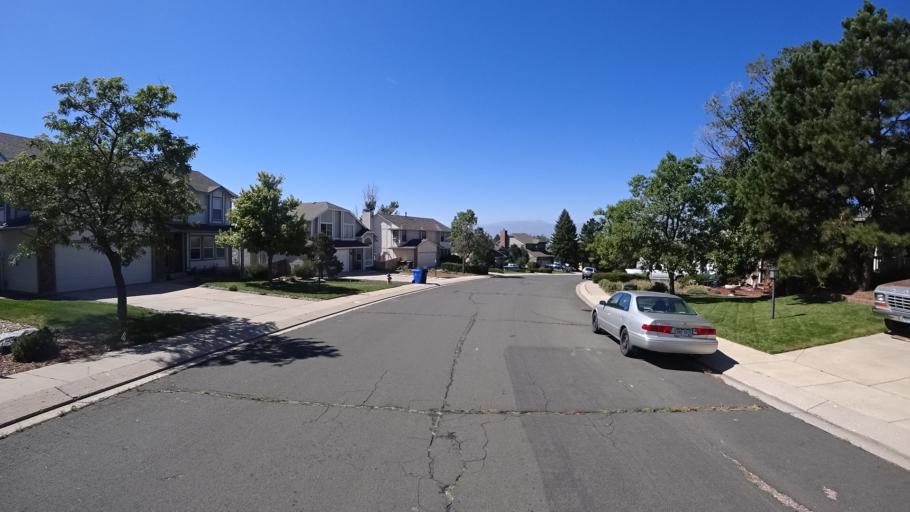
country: US
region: Colorado
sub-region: El Paso County
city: Black Forest
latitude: 38.9438
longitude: -104.7530
